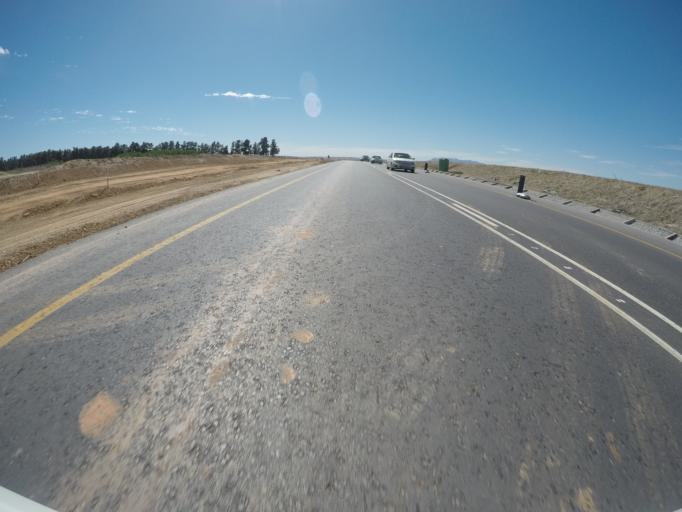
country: ZA
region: Western Cape
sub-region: West Coast District Municipality
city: Malmesbury
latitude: -33.5016
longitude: 18.6634
